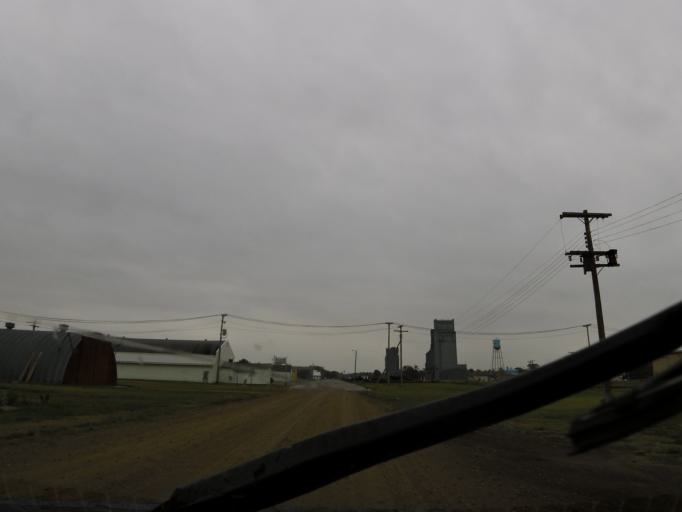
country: US
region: Minnesota
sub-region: Marshall County
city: Warren
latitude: 48.4540
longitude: -96.8743
